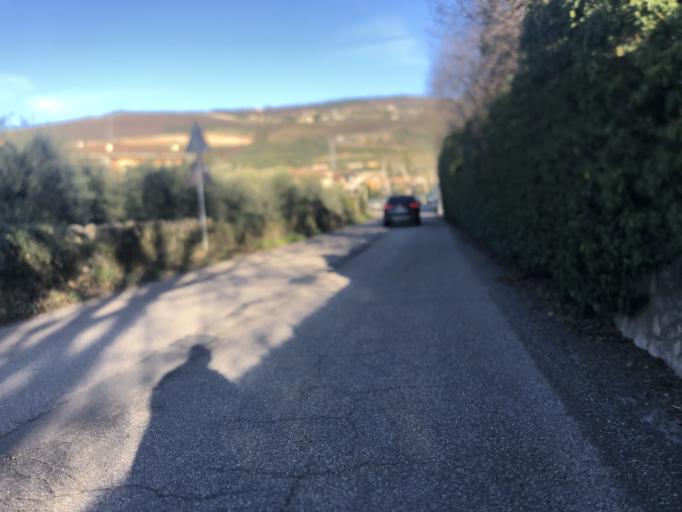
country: IT
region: Veneto
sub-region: Provincia di Verona
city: Fumane
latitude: 45.5347
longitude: 10.8799
